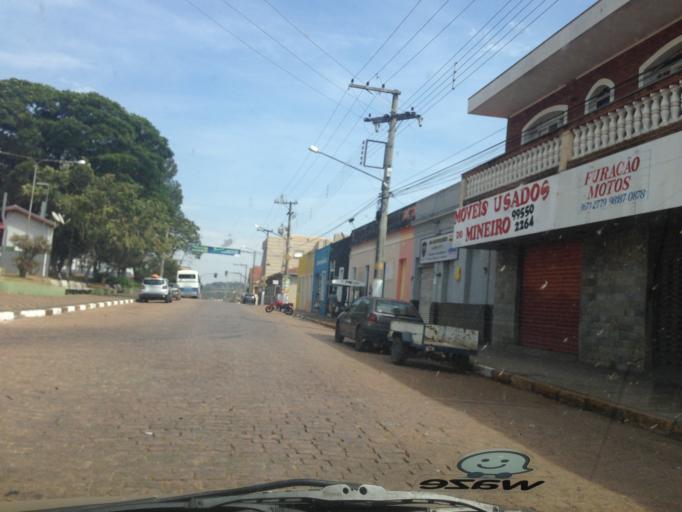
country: BR
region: Sao Paulo
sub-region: Casa Branca
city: Casa Branca
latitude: -21.7787
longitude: -47.0778
